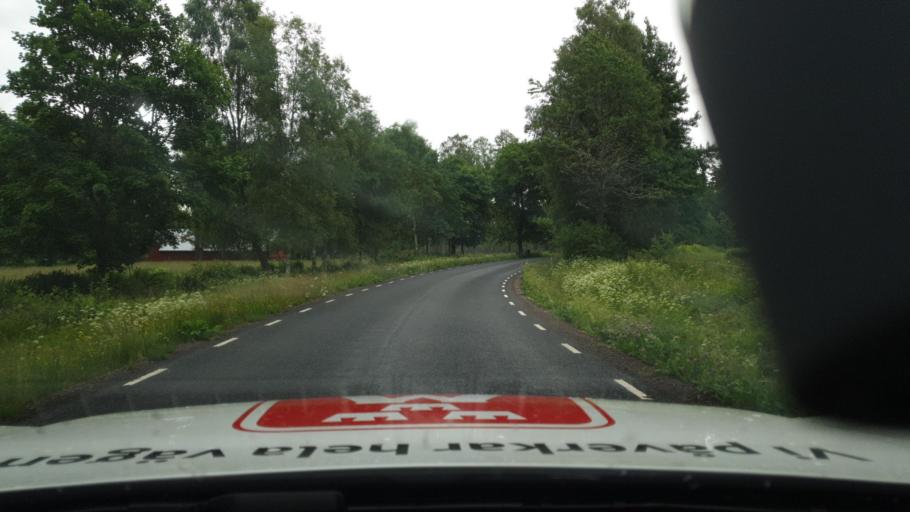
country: SE
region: Joenkoeping
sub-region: Mullsjo Kommun
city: Mullsjoe
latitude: 58.0098
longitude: 13.7129
